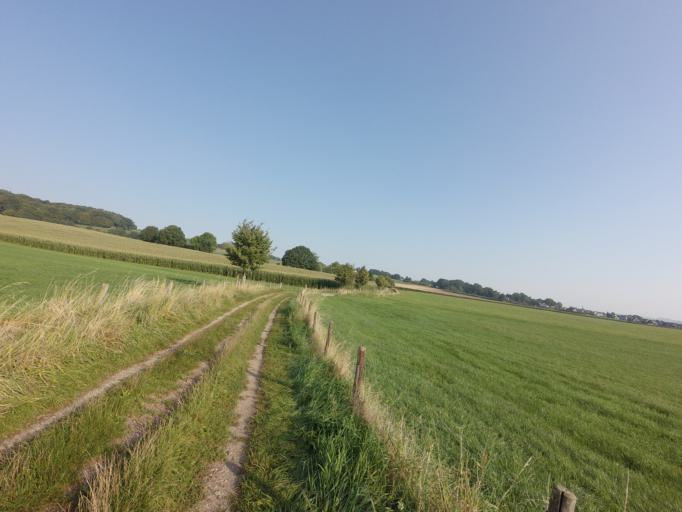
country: BE
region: Wallonia
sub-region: Province de Liege
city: Plombieres
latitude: 50.7679
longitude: 5.9085
